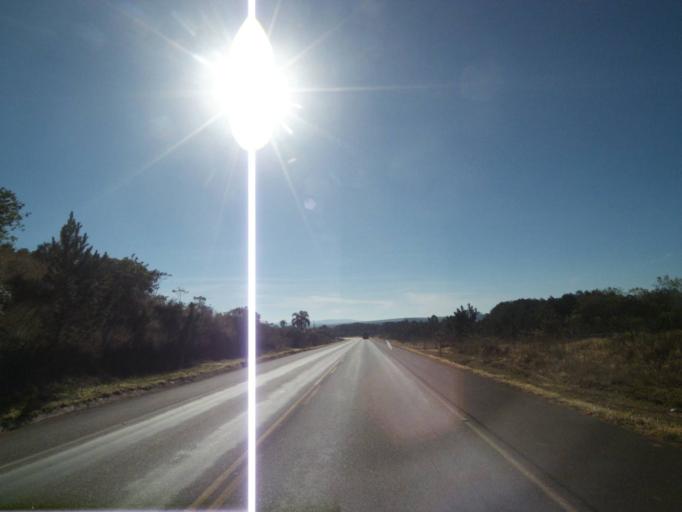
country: BR
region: Parana
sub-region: Tibagi
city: Tibagi
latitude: -24.4918
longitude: -50.4413
